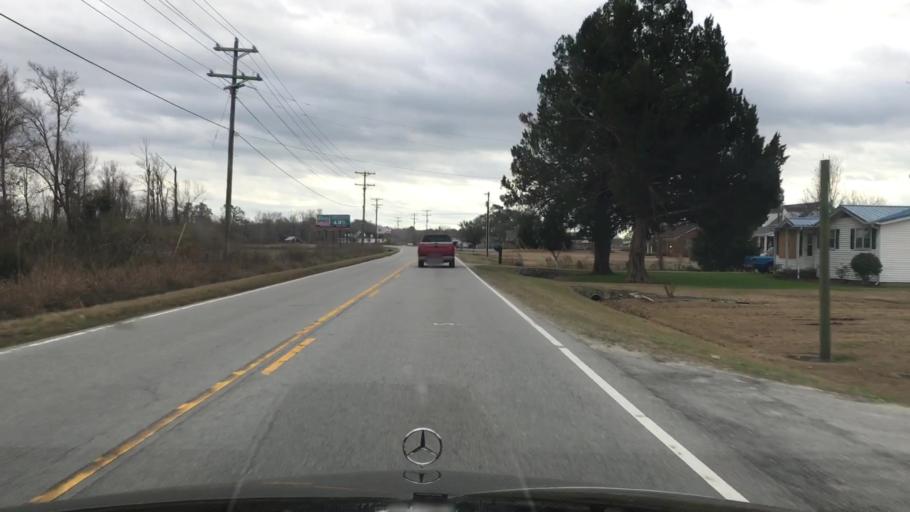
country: US
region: North Carolina
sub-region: Onslow County
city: Half Moon
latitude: 34.8491
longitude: -77.4813
